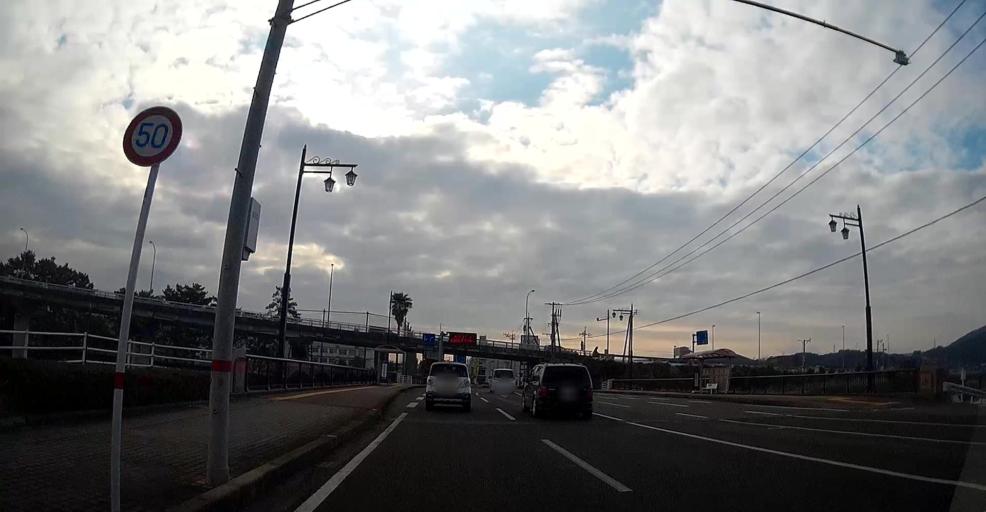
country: JP
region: Kumamoto
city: Hondo
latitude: 32.4478
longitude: 130.2005
